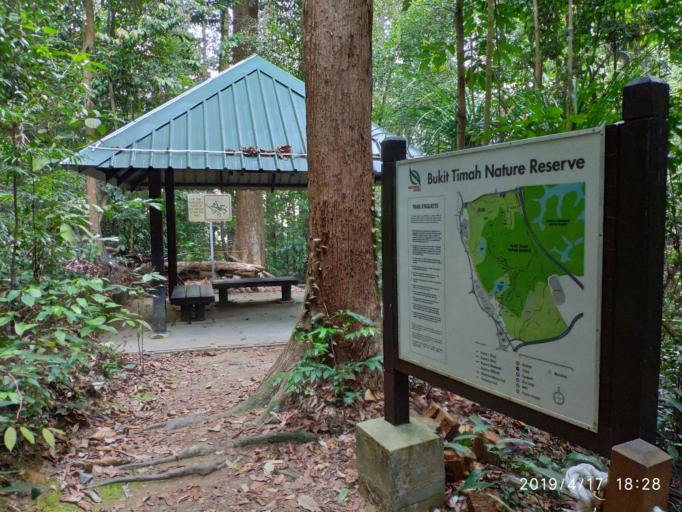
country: SG
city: Singapore
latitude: 1.3559
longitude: 103.7738
